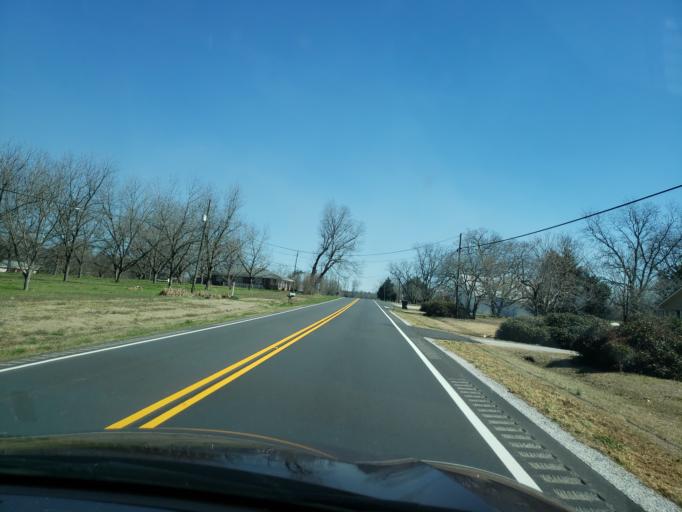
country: US
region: Alabama
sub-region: Elmore County
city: Tallassee
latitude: 32.5821
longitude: -85.7387
